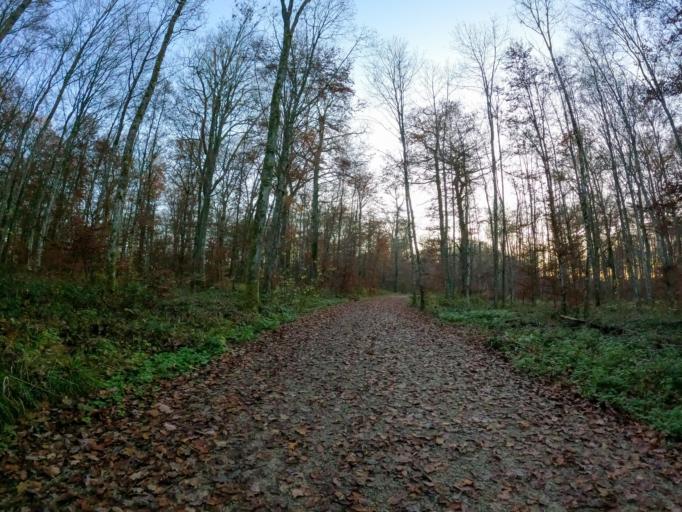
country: LU
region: Luxembourg
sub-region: Canton de Luxembourg
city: Bertrange
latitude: 49.5889
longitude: 6.0422
